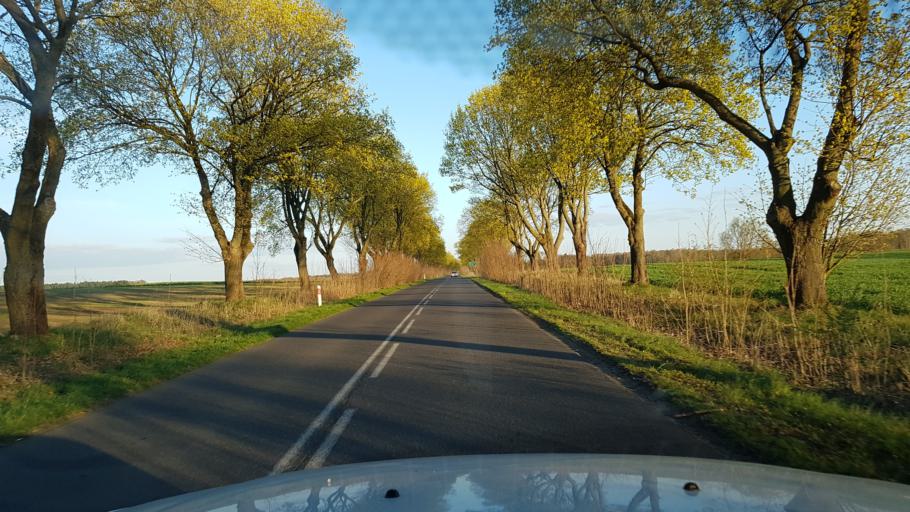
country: PL
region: West Pomeranian Voivodeship
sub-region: Powiat stargardzki
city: Chociwel
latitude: 53.4554
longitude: 15.3394
